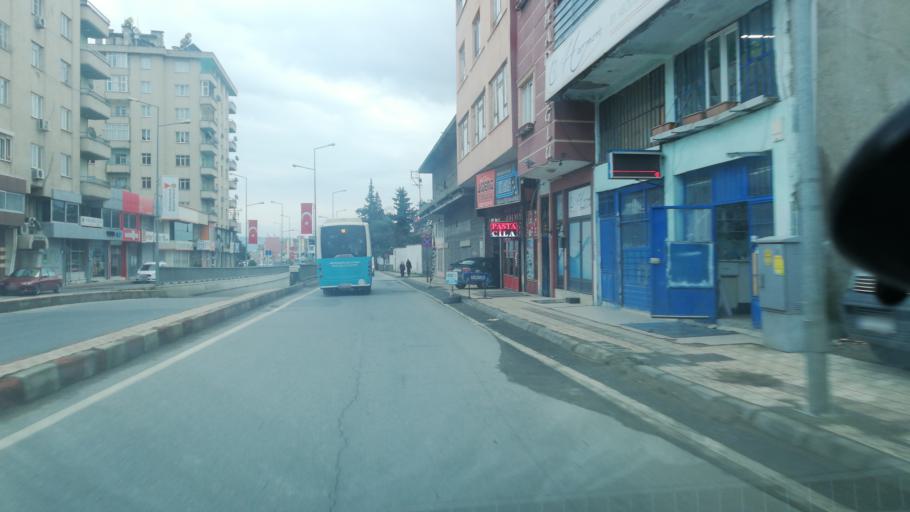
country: TR
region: Kahramanmaras
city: Kahramanmaras
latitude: 37.5725
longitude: 36.9404
